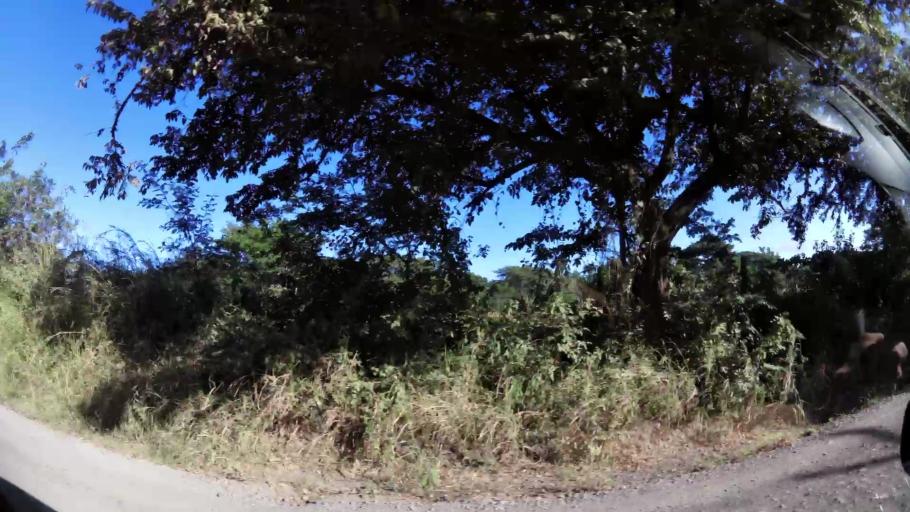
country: CR
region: Guanacaste
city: Sardinal
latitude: 10.4805
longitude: -85.6069
